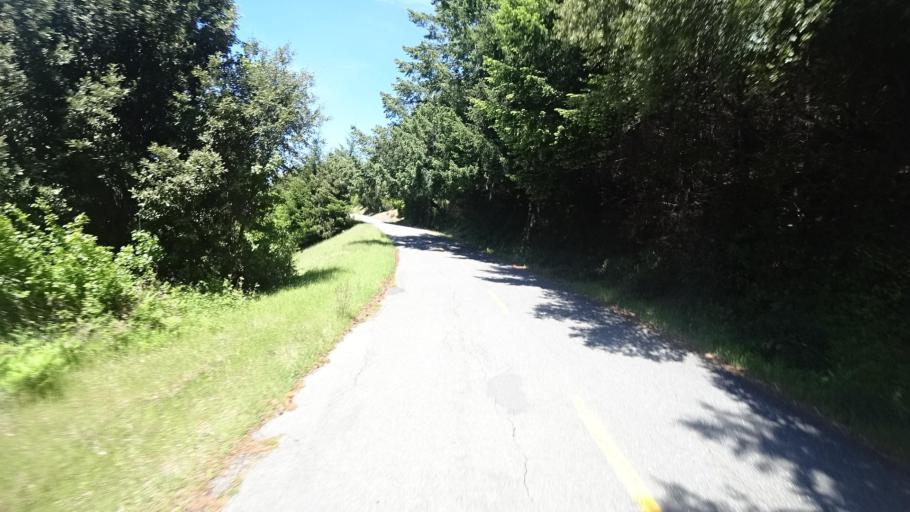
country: US
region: California
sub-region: Humboldt County
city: Rio Dell
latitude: 40.2543
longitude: -124.1178
